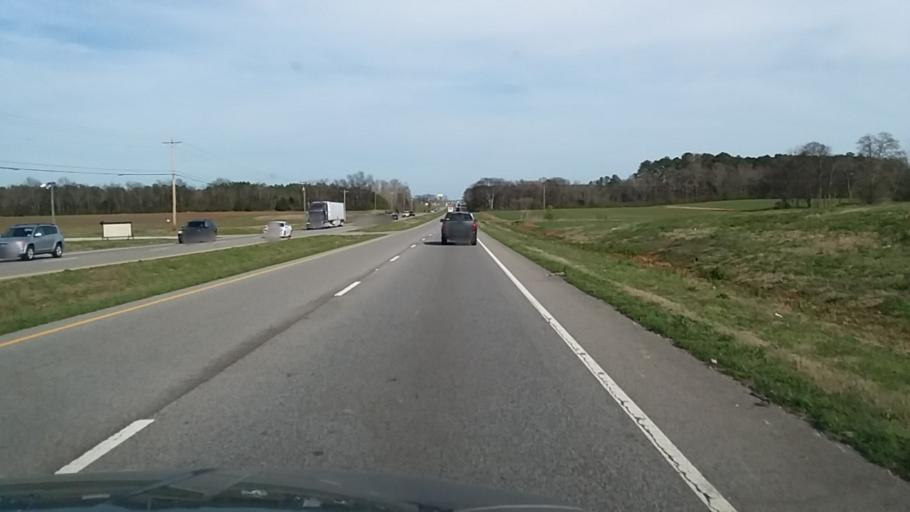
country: US
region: Alabama
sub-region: Morgan County
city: Decatur
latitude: 34.6283
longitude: -86.9309
